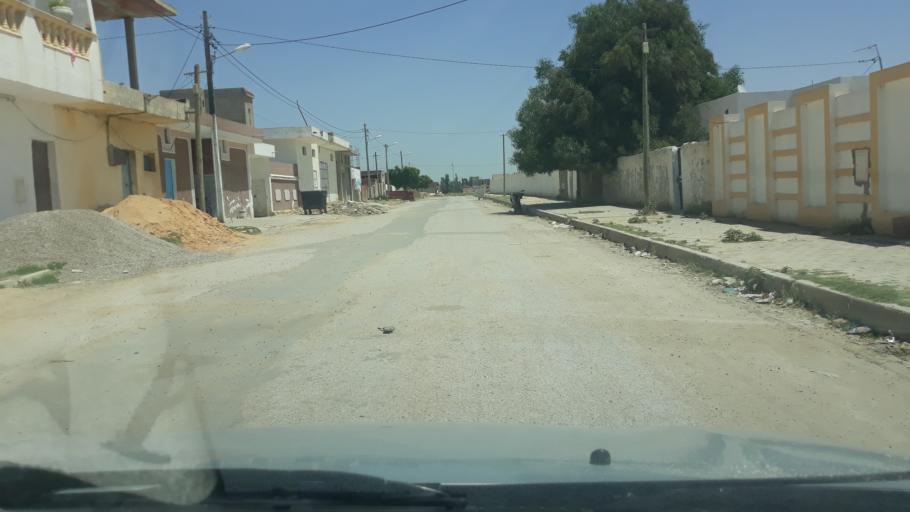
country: TN
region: Al Qayrawan
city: Kairouan
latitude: 35.6178
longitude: 9.9285
